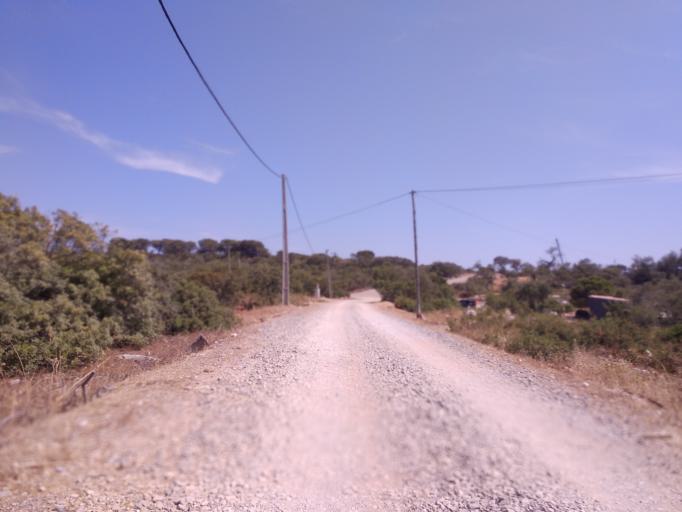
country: PT
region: Faro
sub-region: Faro
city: Santa Barbara de Nexe
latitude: 37.0931
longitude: -7.9745
